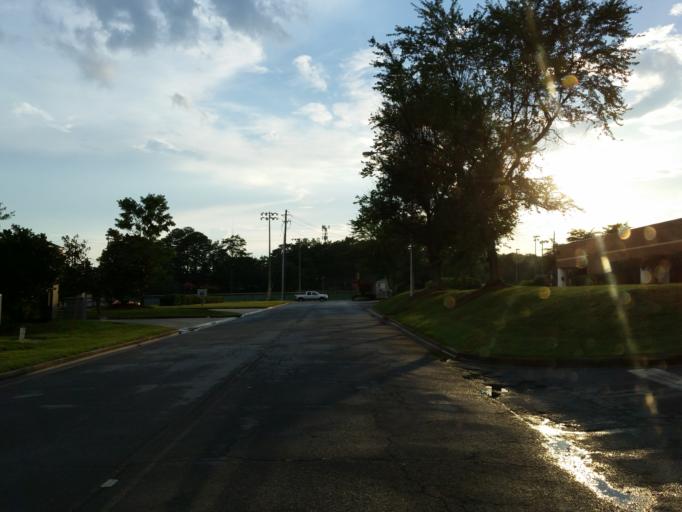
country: US
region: Georgia
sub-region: Cobb County
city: Marietta
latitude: 33.9395
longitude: -84.5337
